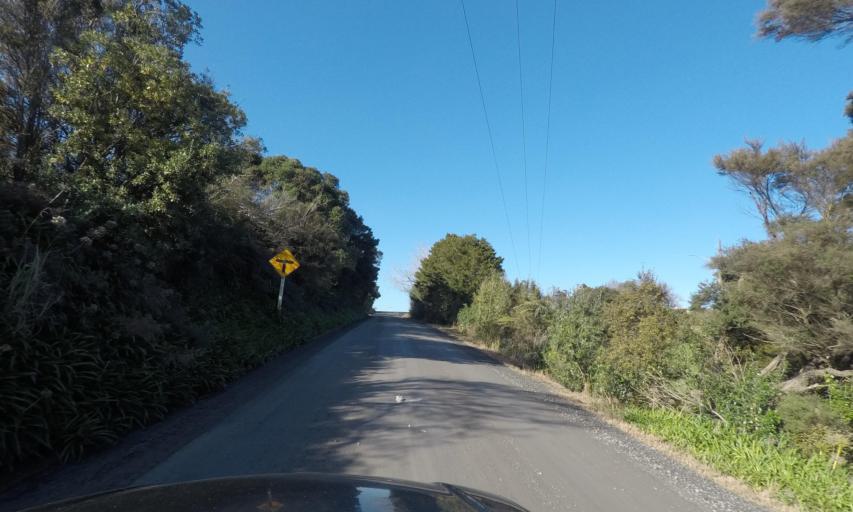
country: NZ
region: Auckland
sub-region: Auckland
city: Wellsford
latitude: -36.1606
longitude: 174.6033
